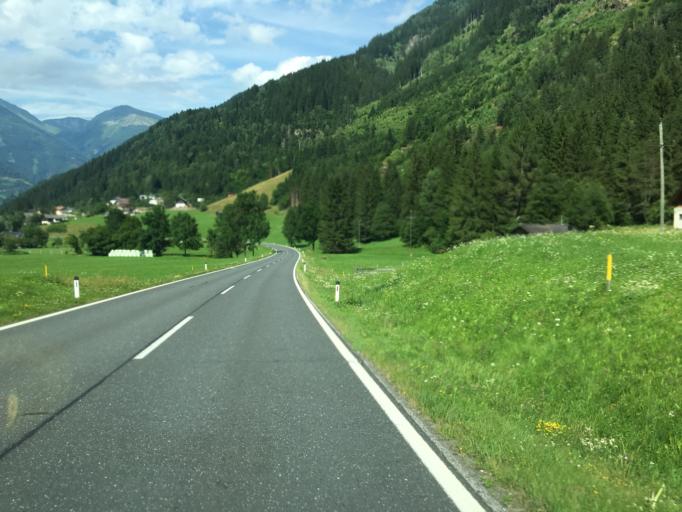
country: AT
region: Carinthia
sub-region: Politischer Bezirk Spittal an der Drau
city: Stall
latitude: 46.8993
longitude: 13.0657
